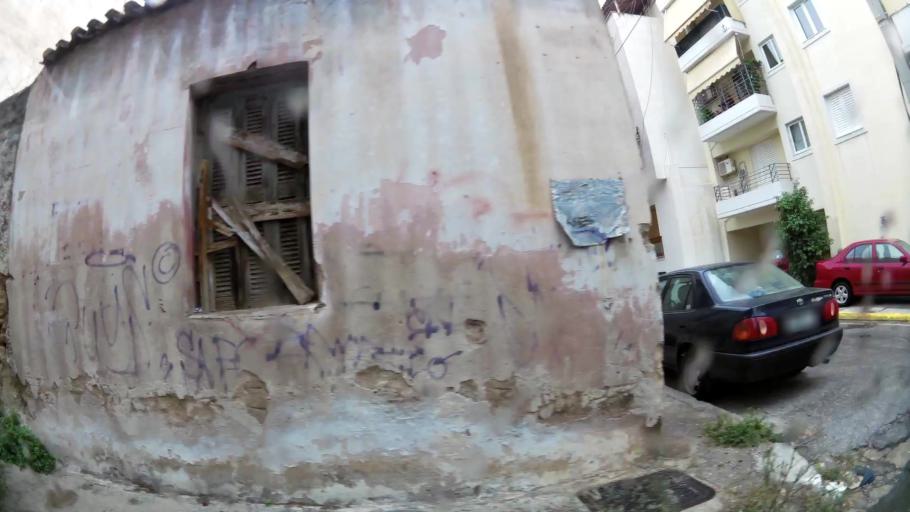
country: GR
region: Attica
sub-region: Nomos Piraios
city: Nikaia
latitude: 37.9589
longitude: 23.6488
